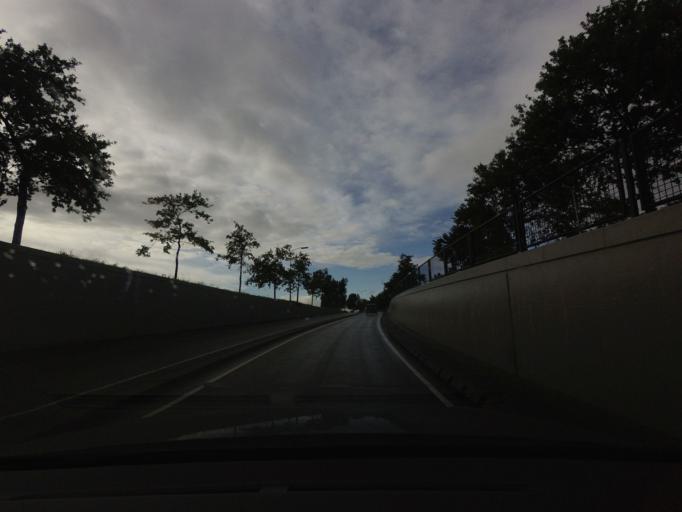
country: NL
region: South Holland
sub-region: Gemeente Voorschoten
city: Voorschoten
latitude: 52.1268
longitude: 4.4335
